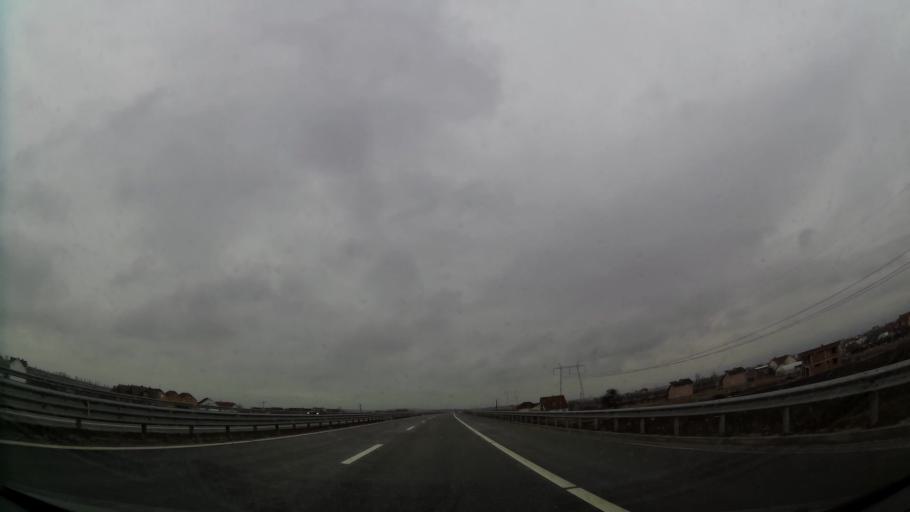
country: XK
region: Ferizaj
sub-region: Komuna e Ferizajt
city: Ferizaj
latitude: 42.4033
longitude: 21.1982
